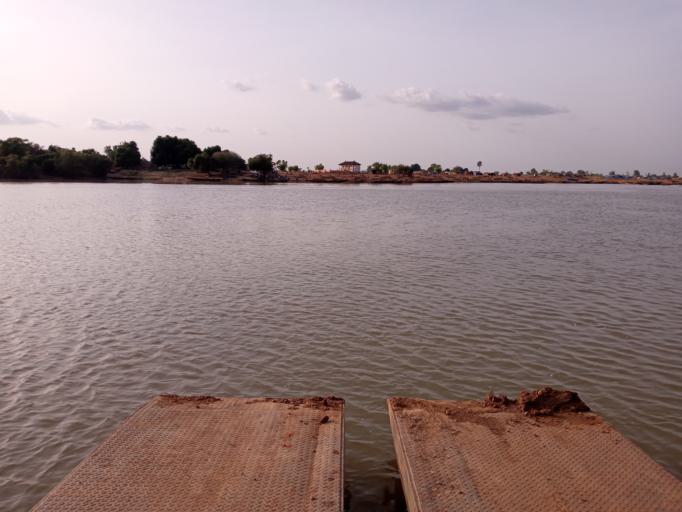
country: ML
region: Koulikoro
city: Kangaba
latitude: 12.1623
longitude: -8.2444
